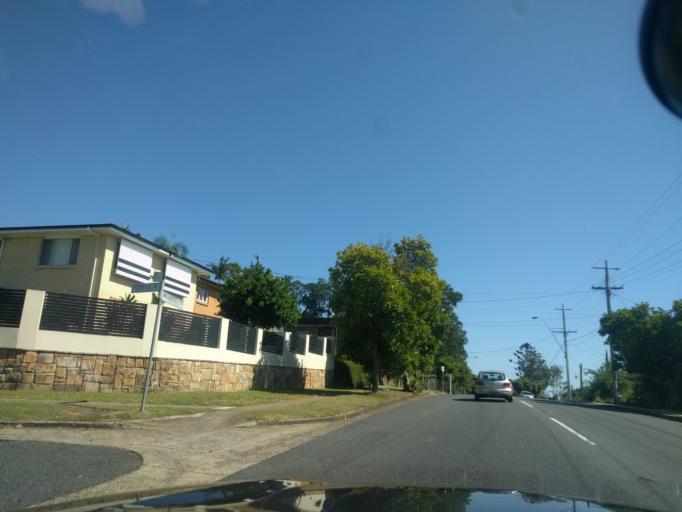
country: AU
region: Queensland
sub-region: Brisbane
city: Chermside West
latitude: -27.3719
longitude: 153.0149
